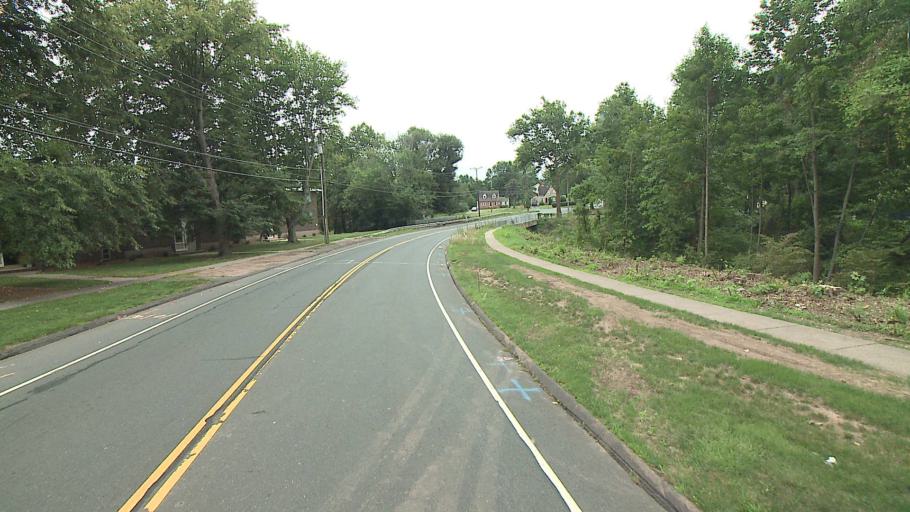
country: US
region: Connecticut
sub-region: Hartford County
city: Wethersfield
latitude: 41.6902
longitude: -72.6588
